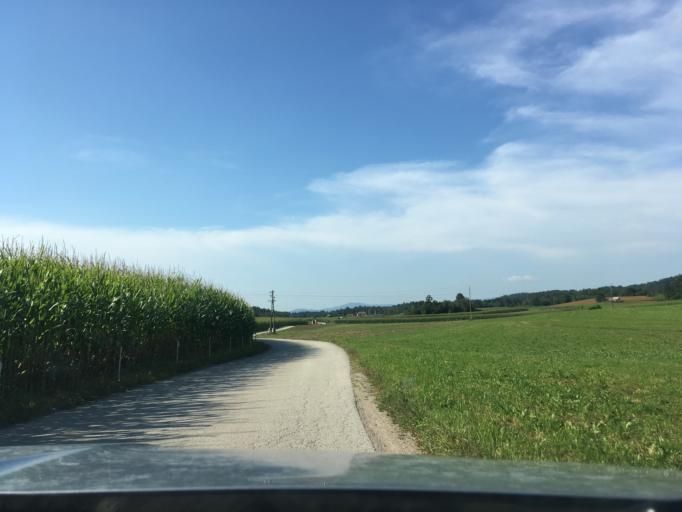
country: SI
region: Crnomelj
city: Crnomelj
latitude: 45.4682
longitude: 15.2097
